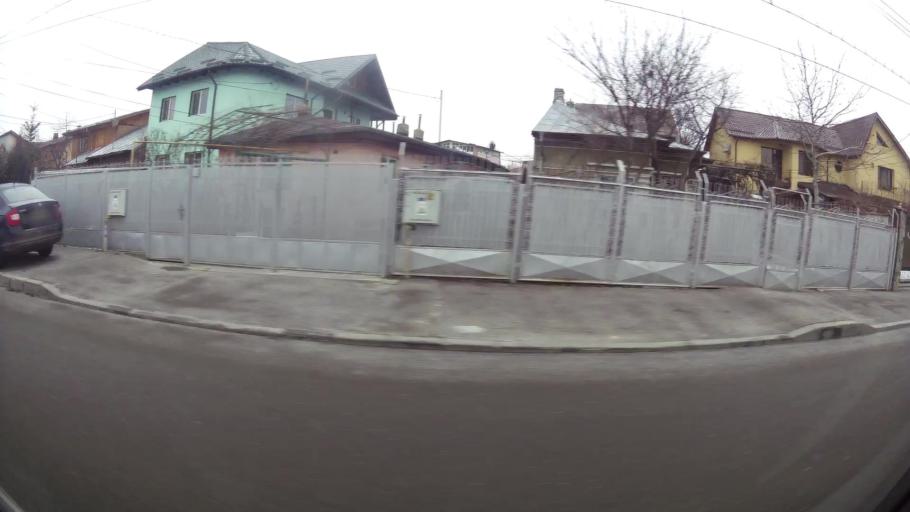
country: RO
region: Prahova
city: Ploiesti
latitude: 44.9426
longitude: 26.0406
